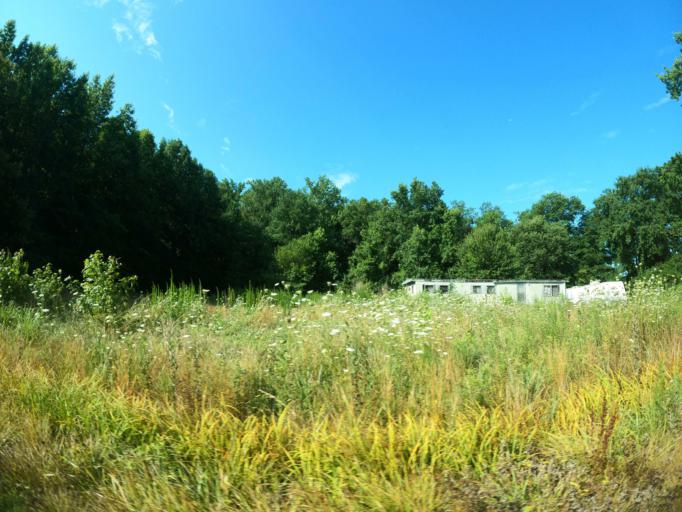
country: US
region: Delaware
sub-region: Sussex County
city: Ocean View
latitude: 38.4934
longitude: -75.1294
